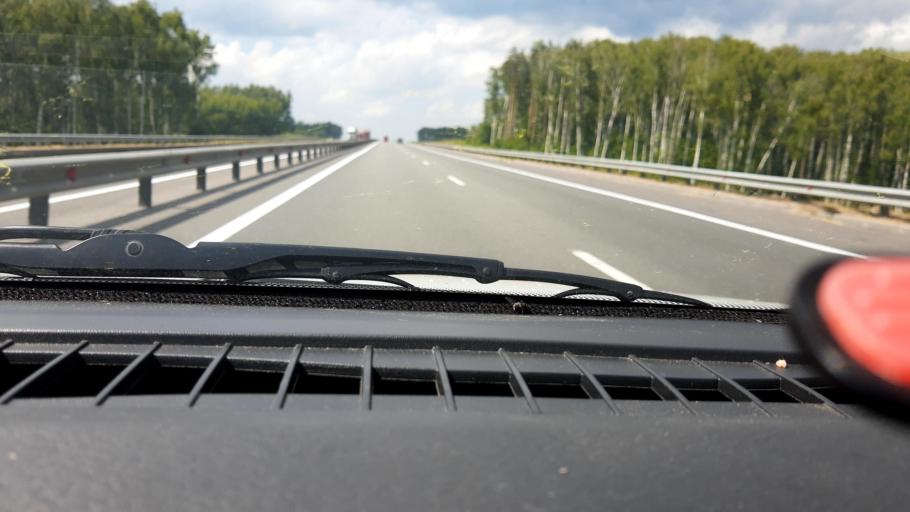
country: RU
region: Nizjnij Novgorod
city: Kstovo
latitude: 56.0850
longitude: 44.0912
